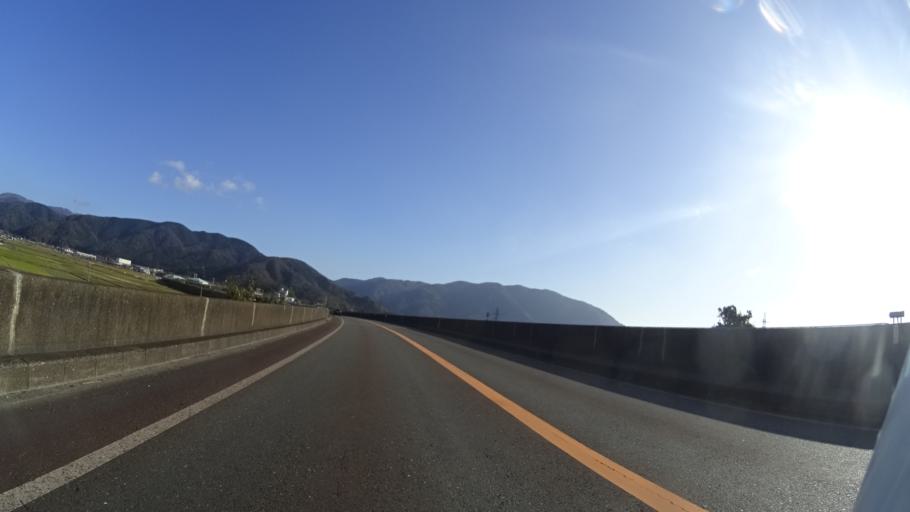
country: JP
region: Fukui
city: Tsuruga
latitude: 35.4556
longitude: 136.0429
